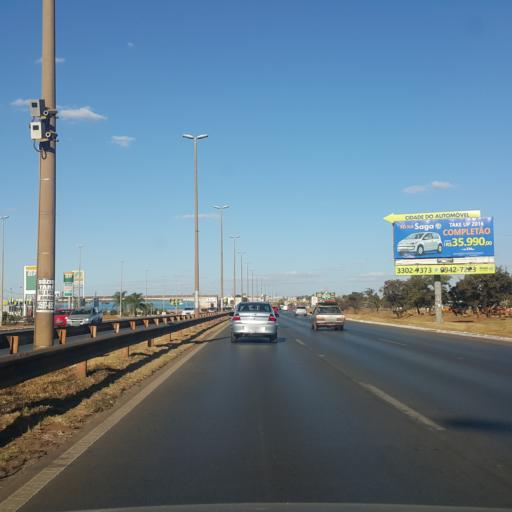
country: BR
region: Federal District
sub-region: Brasilia
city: Brasilia
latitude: -15.7878
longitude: -47.9877
